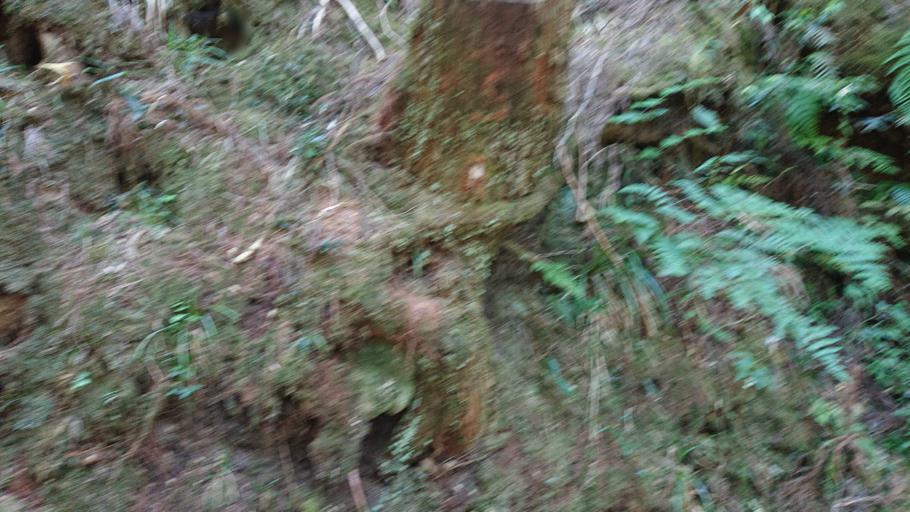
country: TW
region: Taiwan
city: Lugu
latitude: 23.4818
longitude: 120.8246
